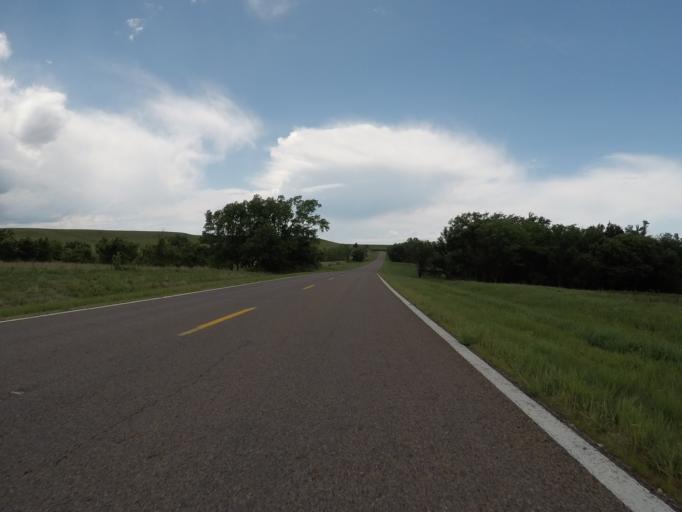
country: US
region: Kansas
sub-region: Wabaunsee County
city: Alma
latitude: 38.8703
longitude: -96.3449
